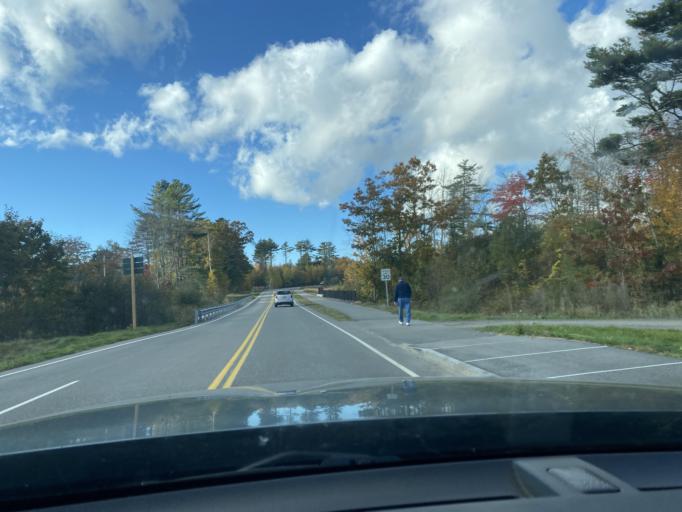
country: US
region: Maine
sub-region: York County
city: York Beach
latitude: 43.1733
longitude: -70.6164
